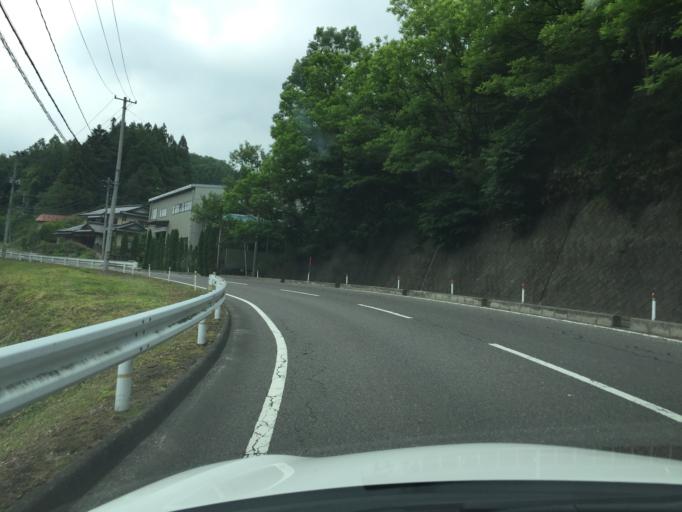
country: JP
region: Fukushima
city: Funehikimachi-funehiki
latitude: 37.2896
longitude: 140.5904
